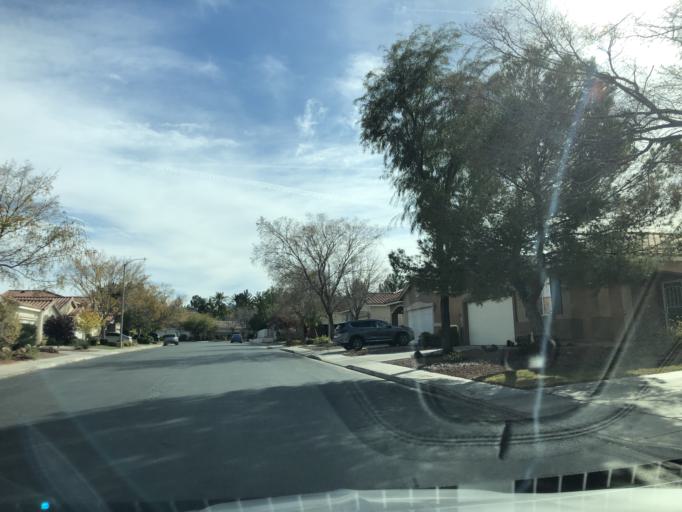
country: US
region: Nevada
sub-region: Clark County
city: Whitney
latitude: 36.0161
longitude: -115.0864
